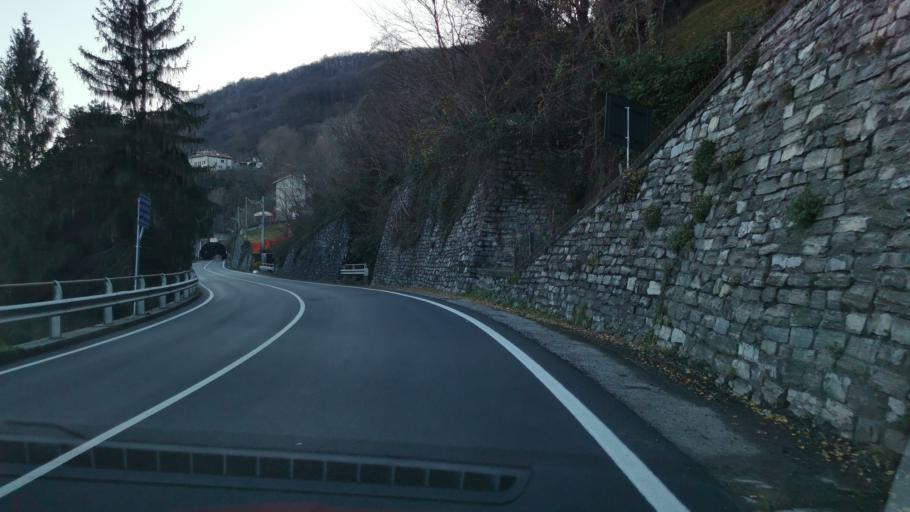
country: IT
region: Lombardy
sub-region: Provincia di Como
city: Vignola
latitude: 46.0834
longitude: 9.2771
